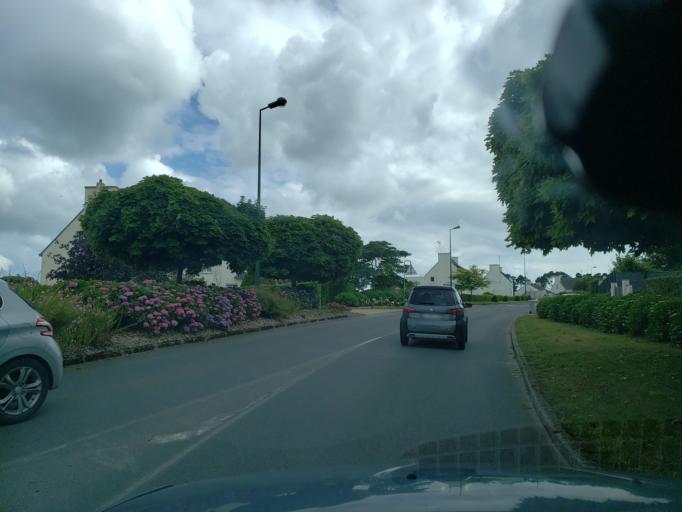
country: FR
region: Brittany
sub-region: Departement du Finistere
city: Plomeur
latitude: 47.8621
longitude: -4.2805
